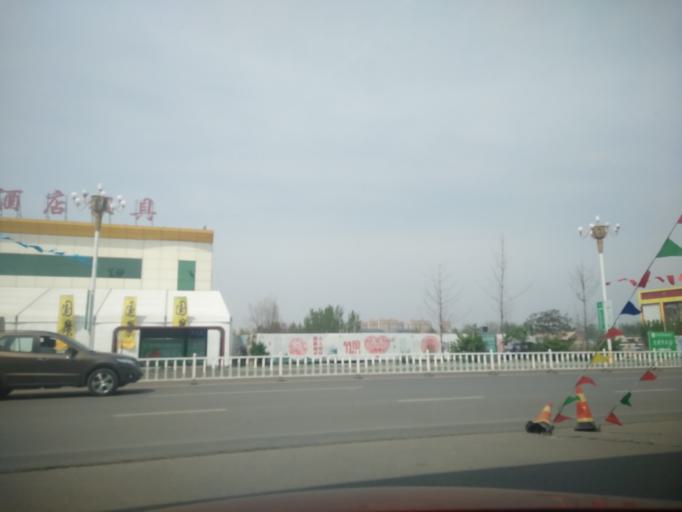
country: CN
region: Tianjin Shi
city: Xiawuqi
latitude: 39.7494
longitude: 117.0178
